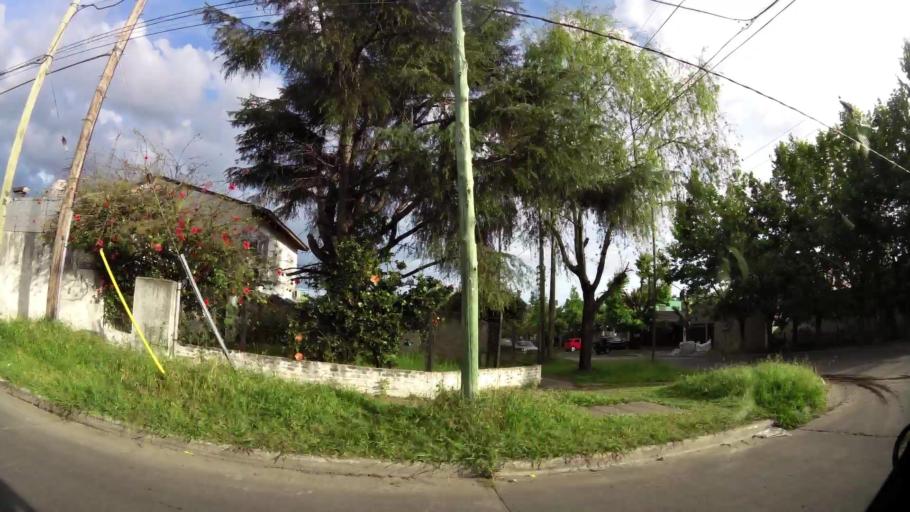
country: AR
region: Buenos Aires
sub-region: Partido de Quilmes
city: Quilmes
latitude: -34.7453
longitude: -58.2540
